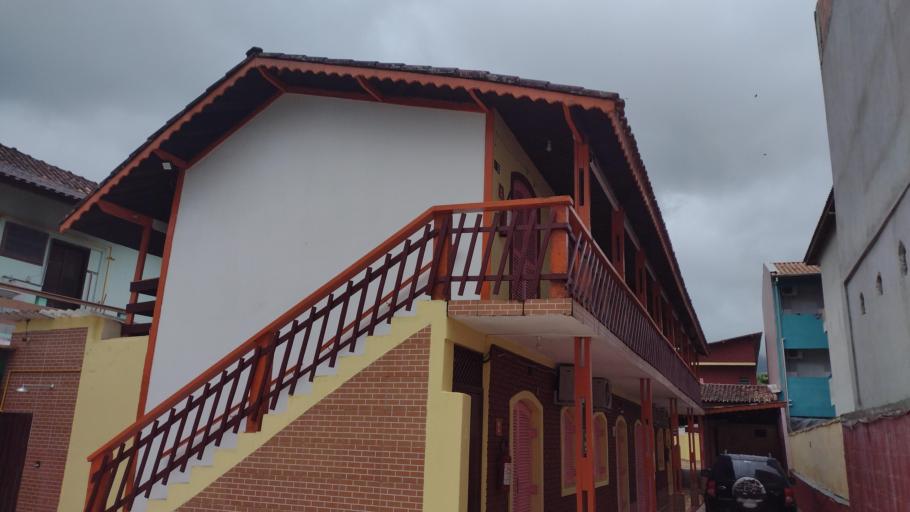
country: BR
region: Sao Paulo
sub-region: Ubatuba
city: Ubatuba
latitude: -23.5434
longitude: -45.2315
